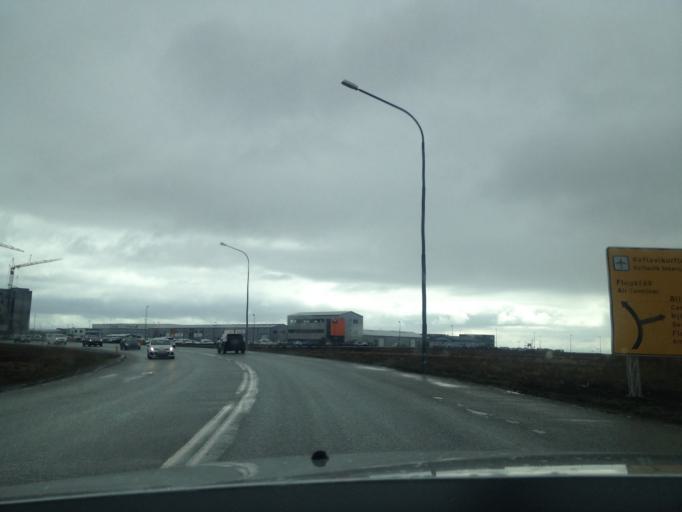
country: IS
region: Southern Peninsula
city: Reykjanesbaer
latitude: 64.0007
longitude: -22.6267
